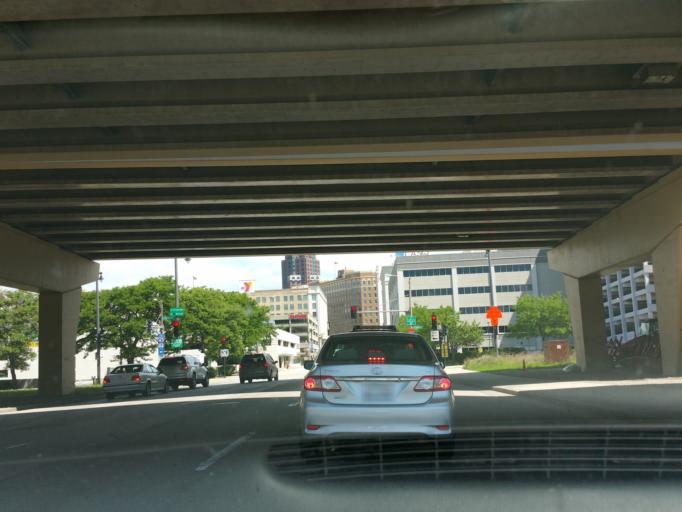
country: US
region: Wisconsin
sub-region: Milwaukee County
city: Milwaukee
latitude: 43.0355
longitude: -87.9111
